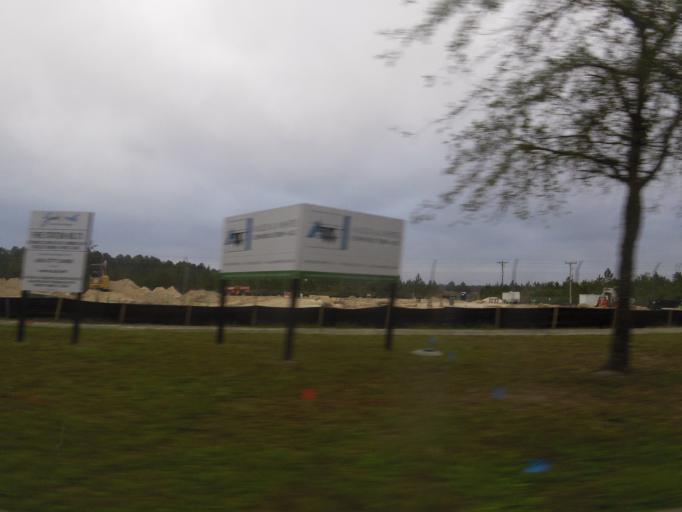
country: US
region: Florida
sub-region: Duval County
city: Baldwin
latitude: 30.2429
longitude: -81.8831
